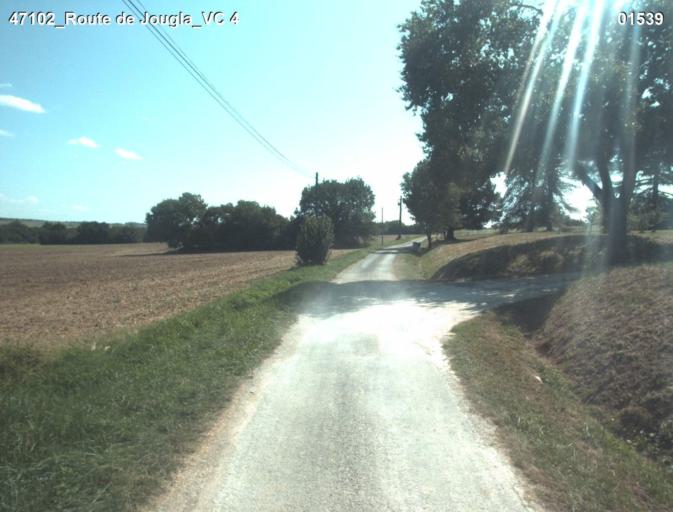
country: FR
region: Aquitaine
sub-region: Departement du Lot-et-Garonne
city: Laplume
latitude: 44.0560
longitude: 0.4363
